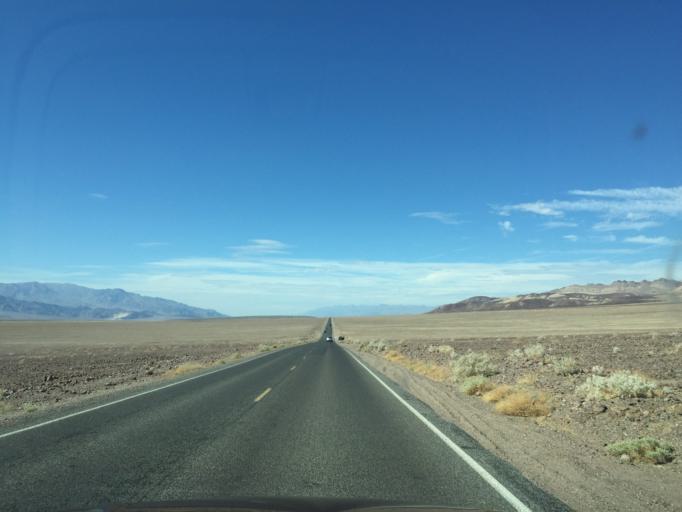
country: US
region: Nevada
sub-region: Nye County
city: Beatty
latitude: 36.2830
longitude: -116.8027
